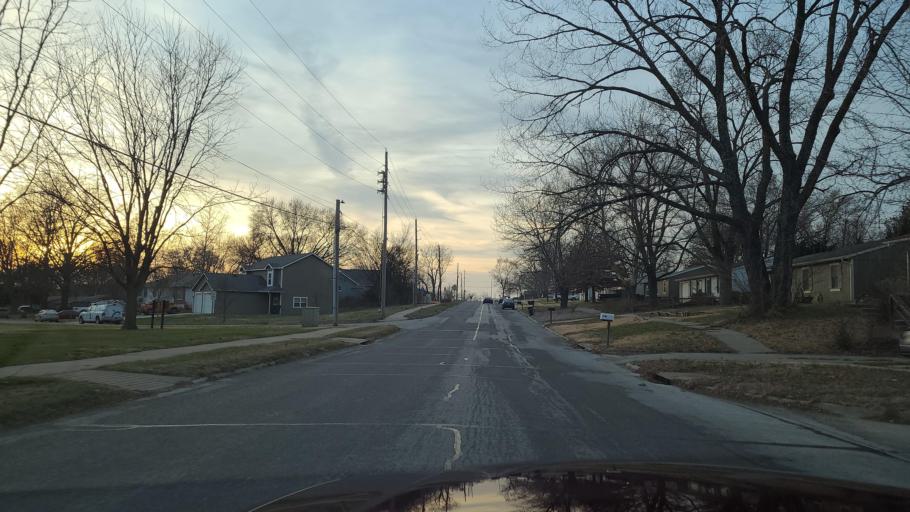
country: US
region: Kansas
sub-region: Douglas County
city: Lawrence
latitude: 38.9354
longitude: -95.2200
